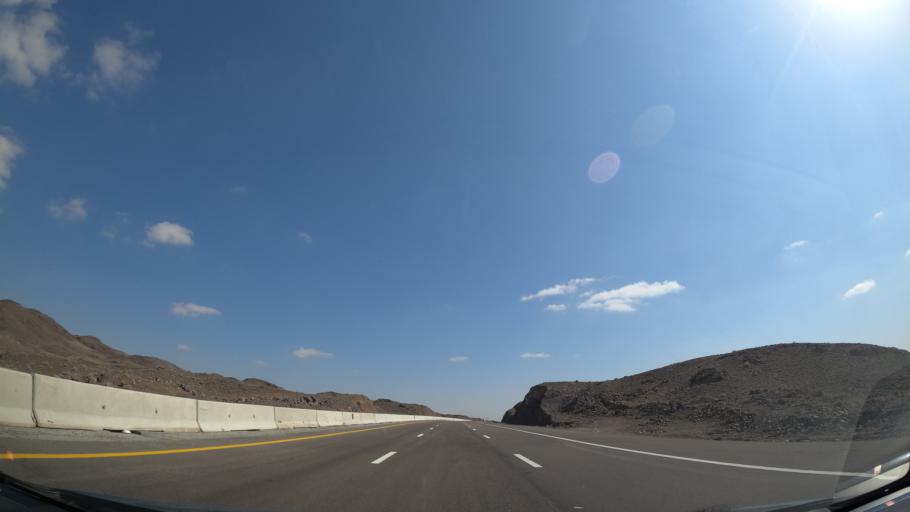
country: IR
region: Alborz
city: Nazarabad
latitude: 35.6607
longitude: 50.6573
